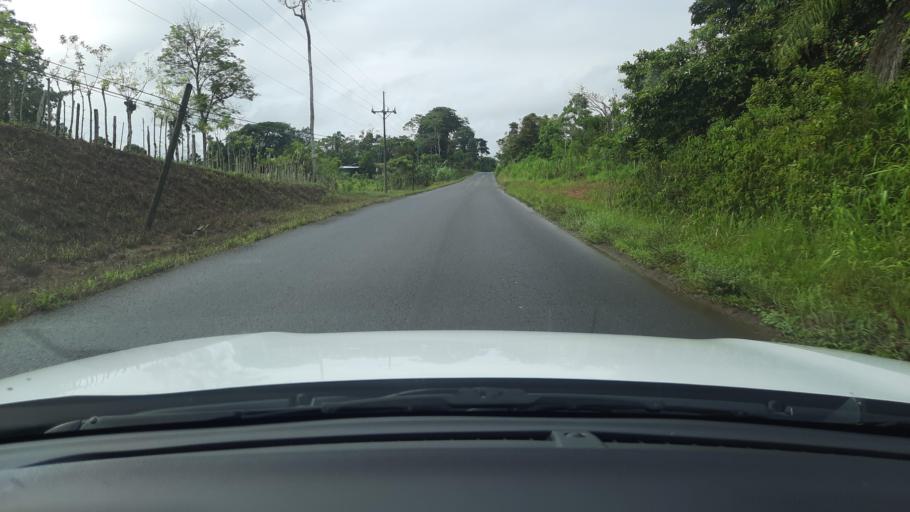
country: CR
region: Alajuela
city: San Jose
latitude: 10.9400
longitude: -85.1109
